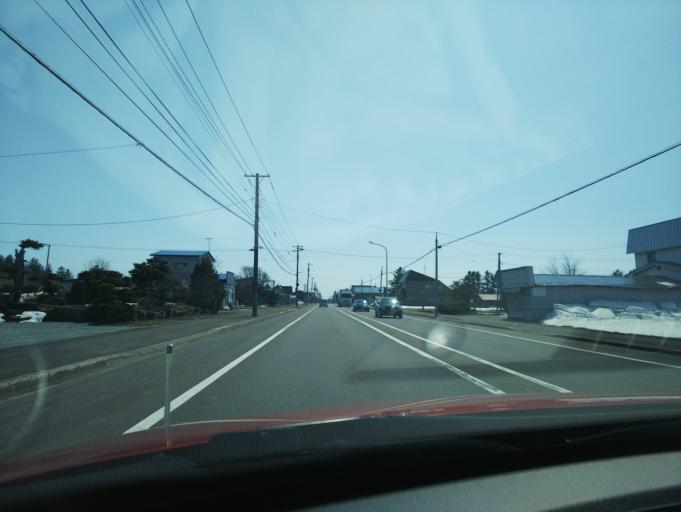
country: JP
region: Hokkaido
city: Nayoro
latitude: 44.2447
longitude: 142.3948
